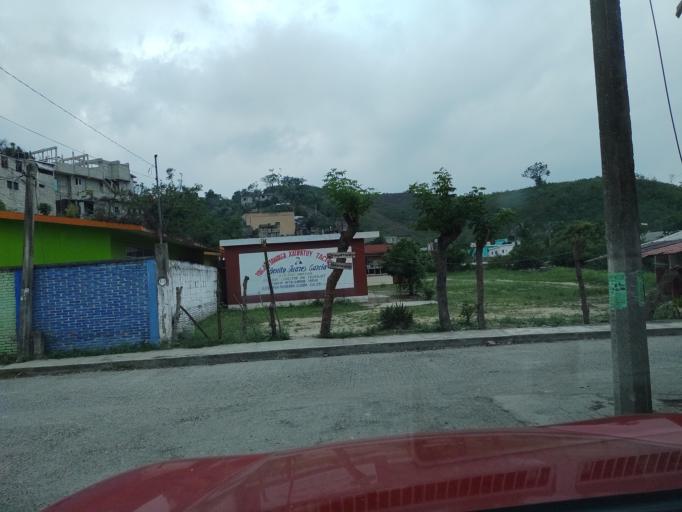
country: MX
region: Veracruz
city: Papantla de Olarte
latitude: 20.4620
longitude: -97.3304
